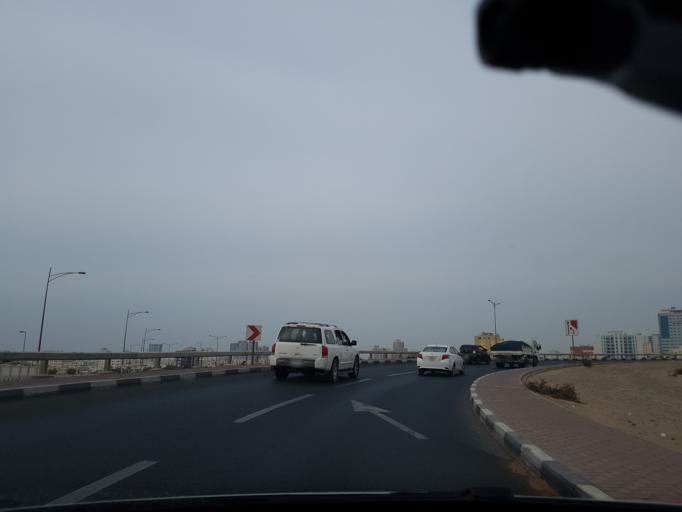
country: AE
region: Ajman
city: Ajman
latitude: 25.3739
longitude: 55.4524
